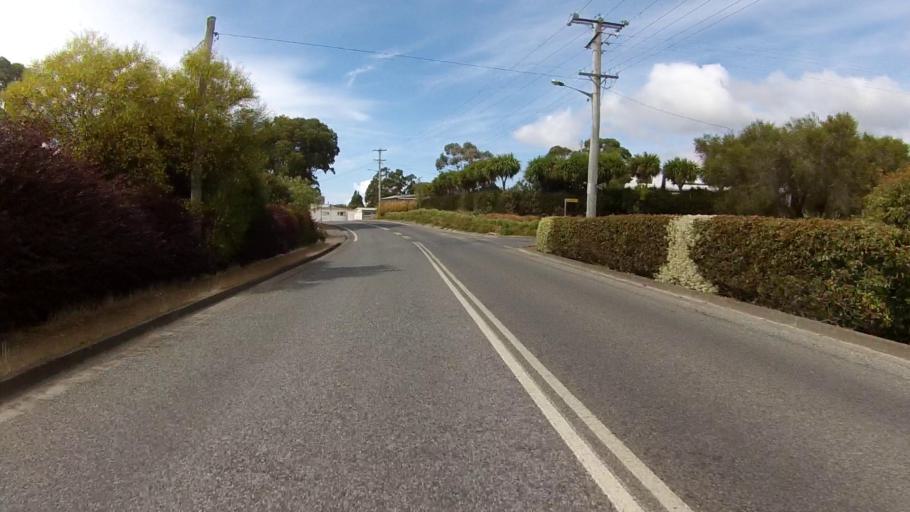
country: AU
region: Tasmania
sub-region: Kingborough
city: Kettering
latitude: -43.1563
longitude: 147.2381
